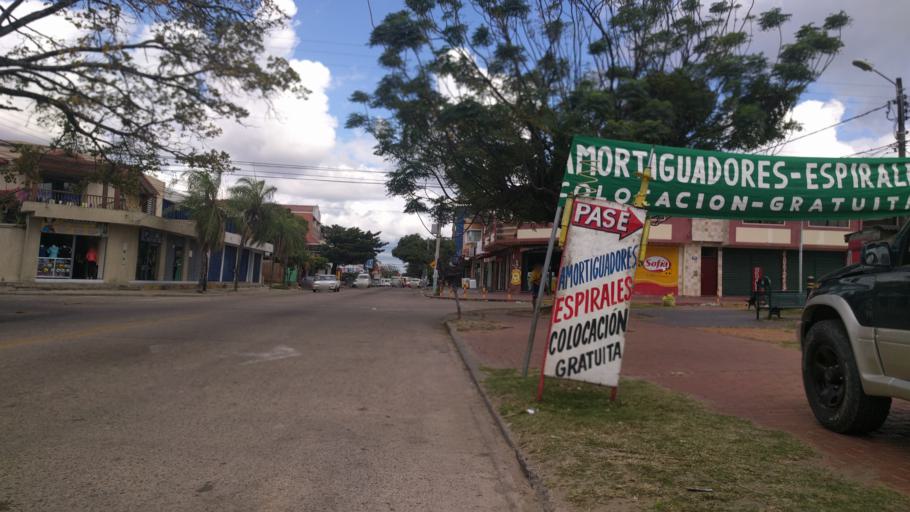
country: BO
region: Santa Cruz
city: Santa Cruz de la Sierra
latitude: -17.8052
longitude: -63.1956
